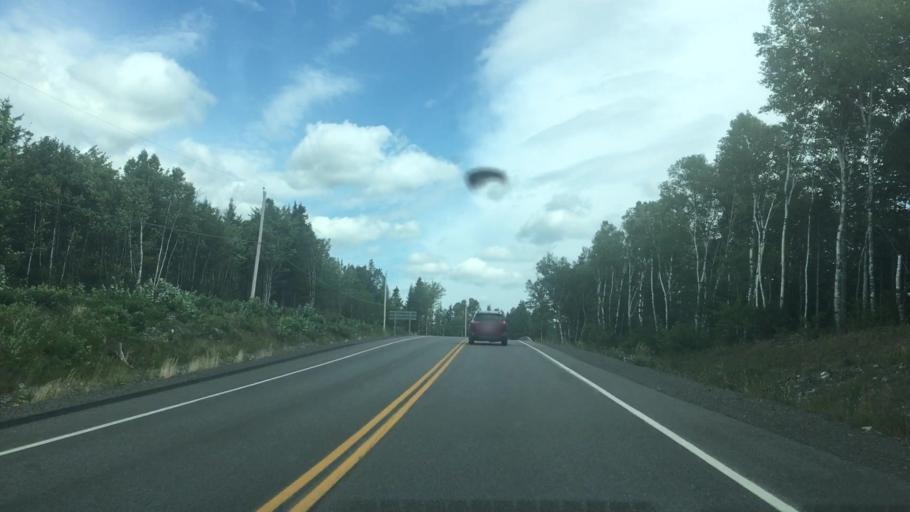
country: CA
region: Nova Scotia
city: Sydney Mines
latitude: 46.3087
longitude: -60.6169
